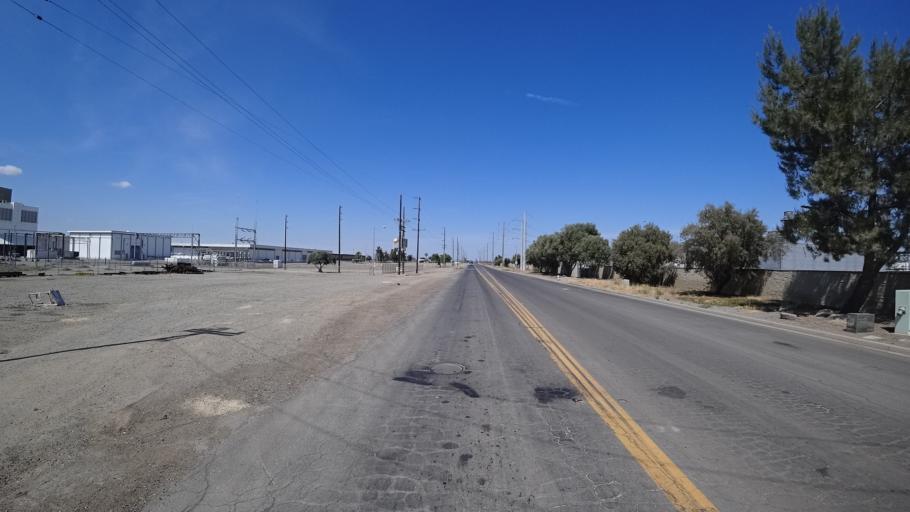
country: US
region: California
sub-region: Kings County
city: Home Garden
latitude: 36.2694
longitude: -119.6463
